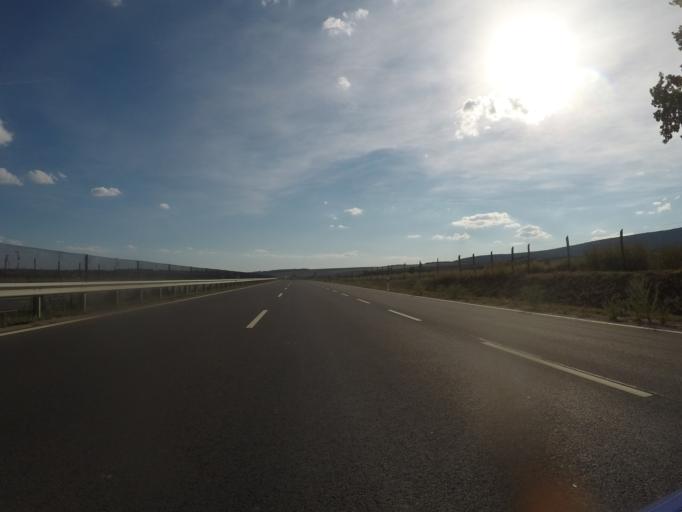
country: HU
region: Nograd
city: Paszto
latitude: 47.9403
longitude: 19.6954
